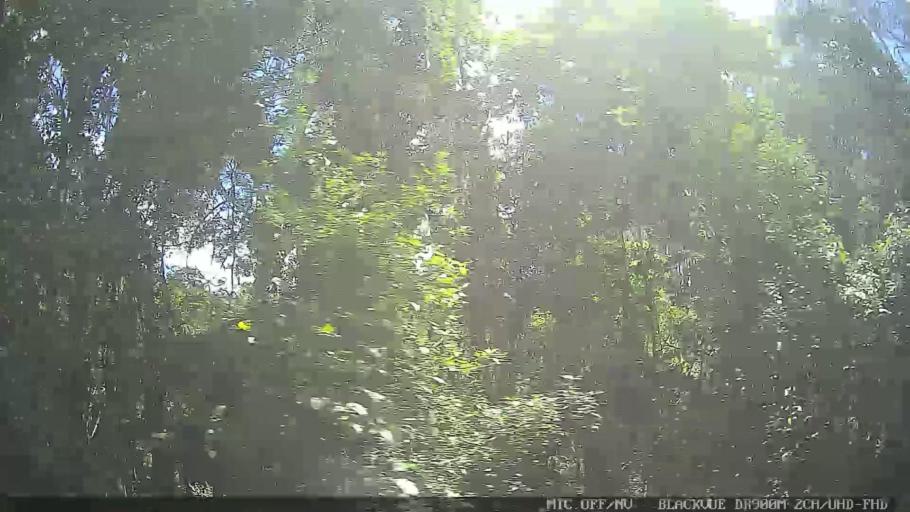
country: BR
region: Sao Paulo
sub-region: Santa Branca
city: Santa Branca
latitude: -23.5406
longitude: -45.6979
